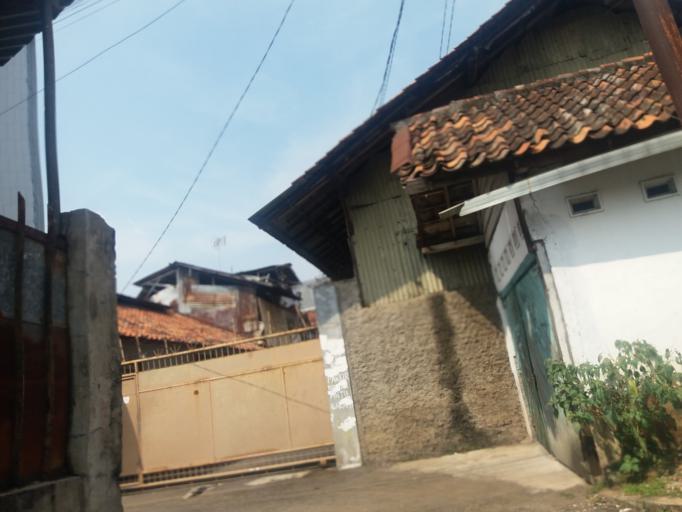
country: ID
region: Jakarta Raya
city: Jakarta
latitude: -6.2234
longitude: 106.8188
